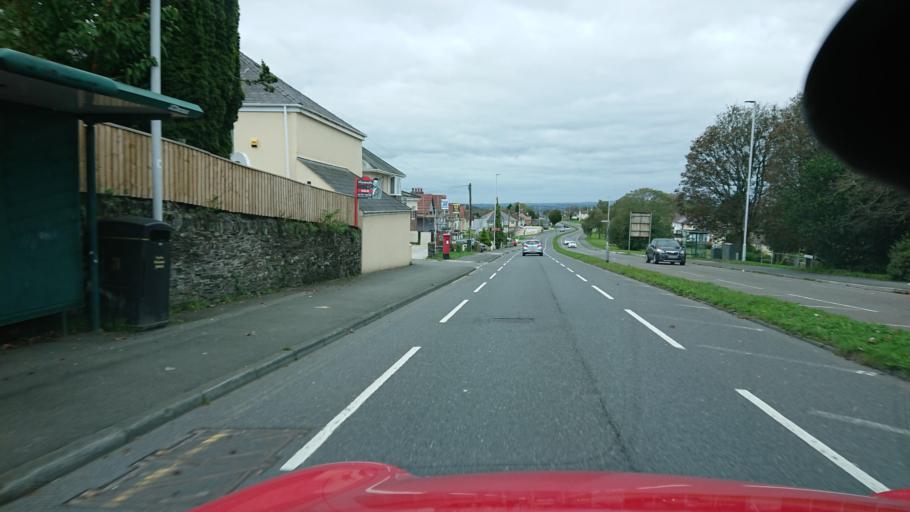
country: GB
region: England
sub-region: Plymouth
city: Plymouth
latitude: 50.4102
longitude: -4.1361
